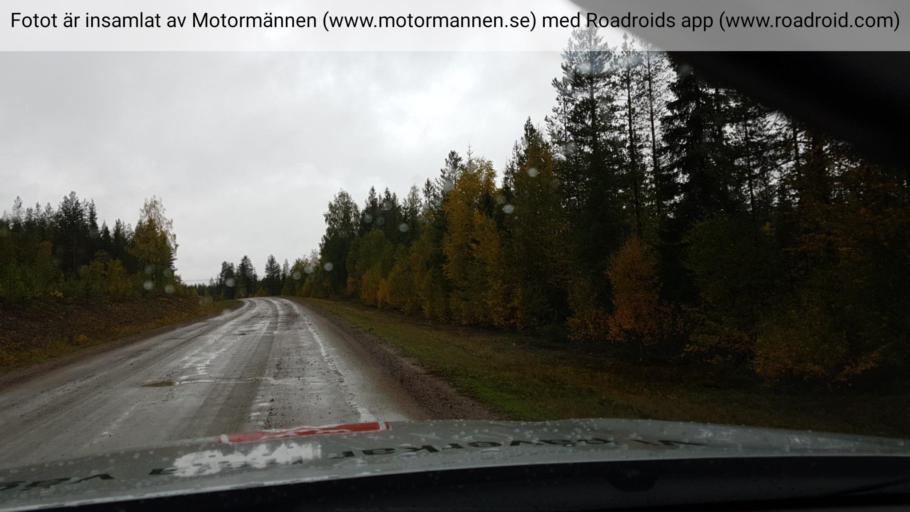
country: SE
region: Norrbotten
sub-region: Alvsbyns Kommun
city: AElvsbyn
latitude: 66.2653
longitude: 21.0638
